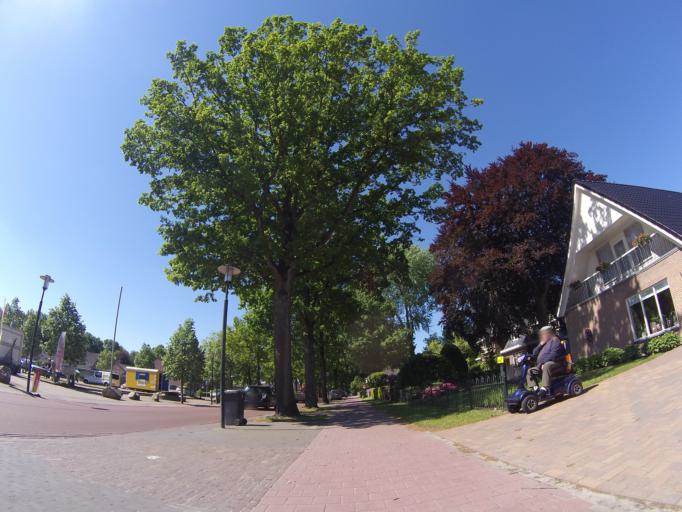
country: NL
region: Drenthe
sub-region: Gemeente Coevorden
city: Sleen
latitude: 52.7913
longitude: 6.7232
